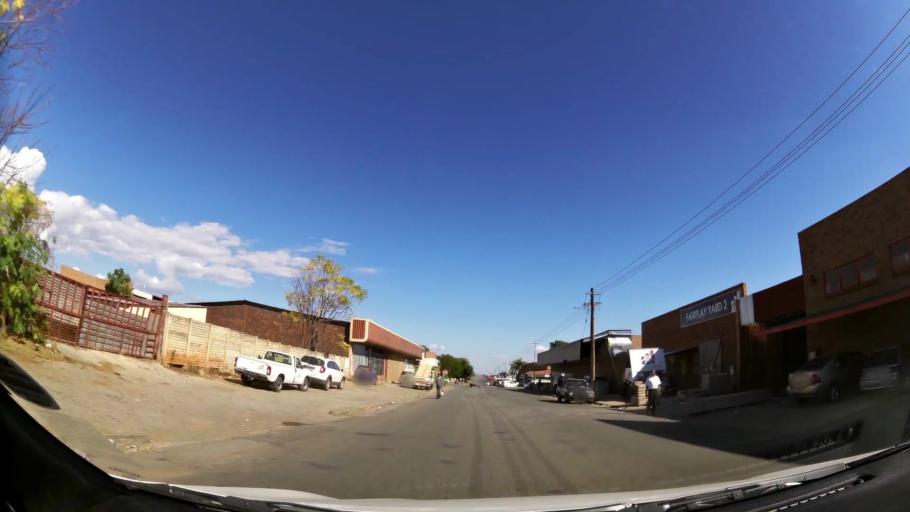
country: ZA
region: Limpopo
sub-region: Waterberg District Municipality
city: Mokopane
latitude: -24.1807
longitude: 29.0162
